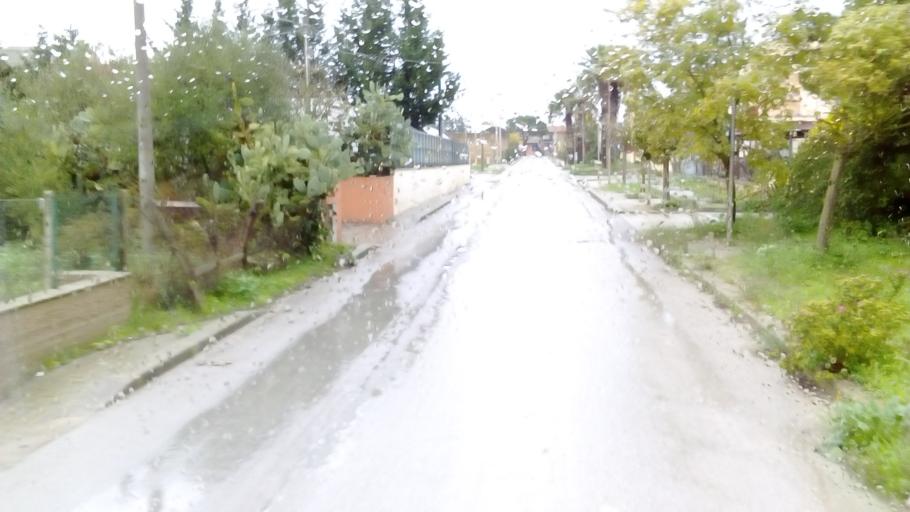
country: IT
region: Sicily
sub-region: Enna
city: Pietraperzia
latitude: 37.4126
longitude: 14.1421
